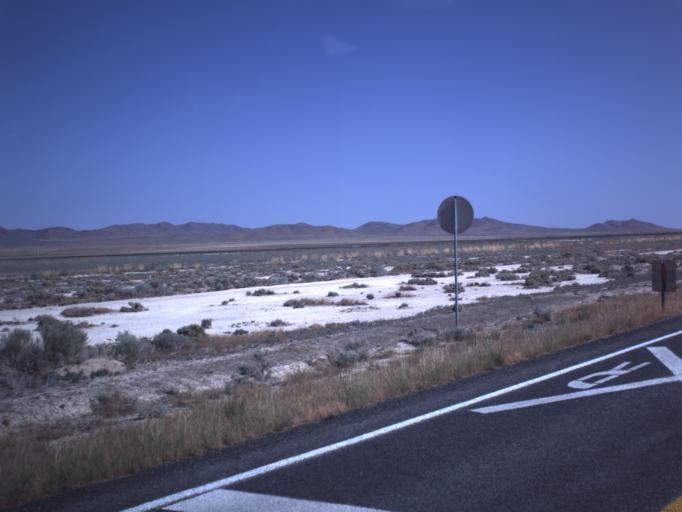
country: US
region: Utah
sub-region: Millard County
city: Delta
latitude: 38.9409
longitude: -112.8079
